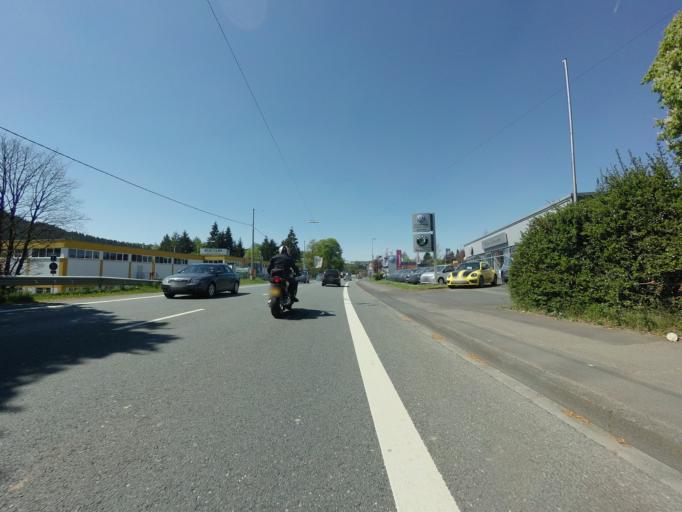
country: DE
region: North Rhine-Westphalia
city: Kreuztal
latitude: 50.9590
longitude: 8.0245
